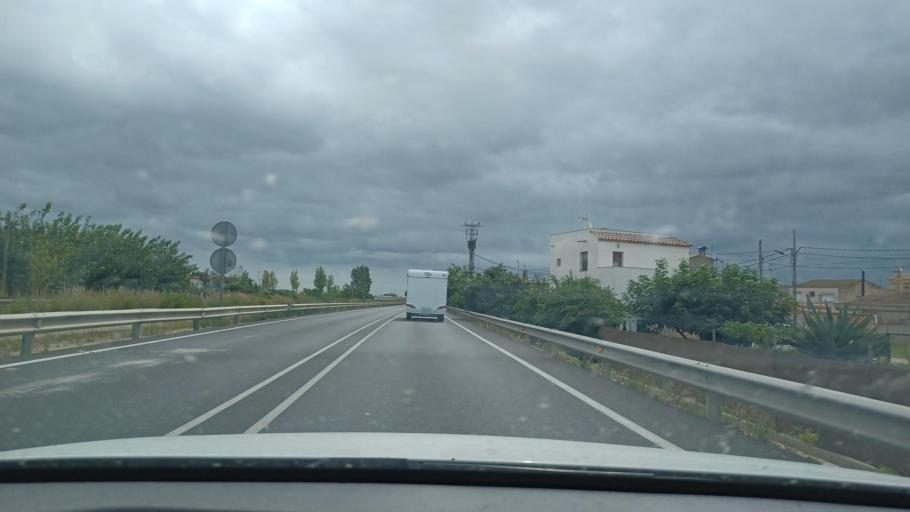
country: ES
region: Catalonia
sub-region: Provincia de Tarragona
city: Deltebre
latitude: 40.7178
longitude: 0.7498
